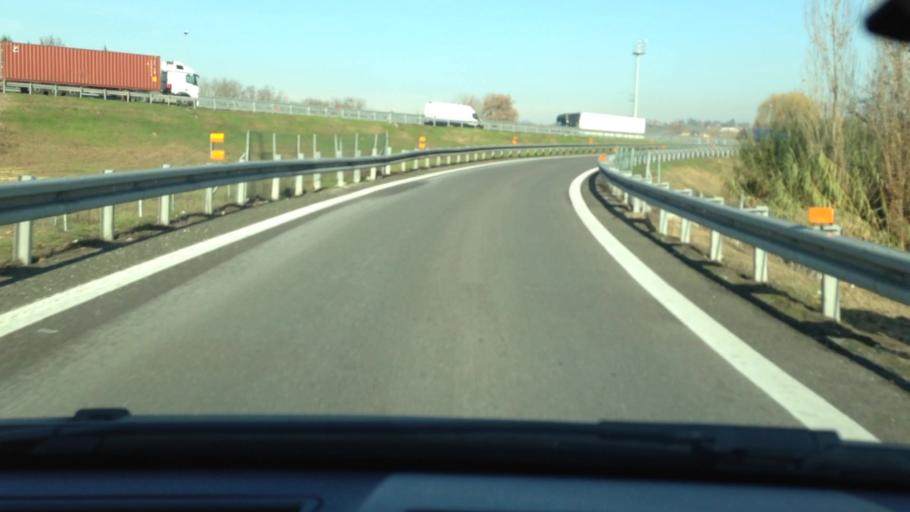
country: IT
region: Piedmont
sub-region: Provincia di Asti
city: Asti
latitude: 44.9076
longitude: 8.1759
